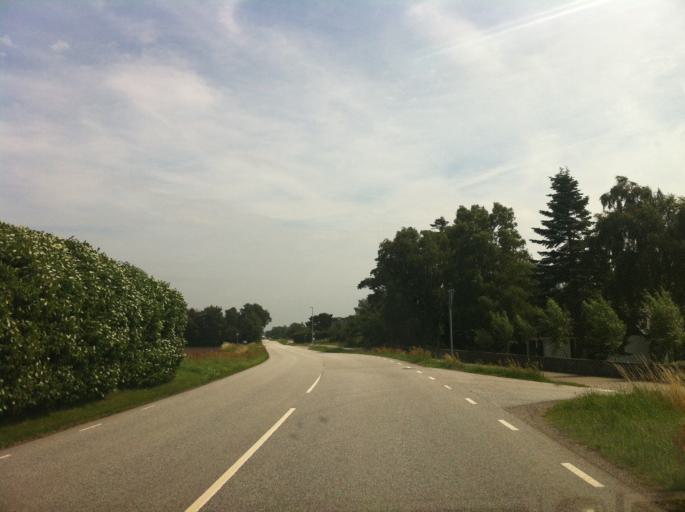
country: SE
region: Skane
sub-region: Trelleborgs Kommun
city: Anderslov
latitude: 55.3475
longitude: 13.2731
